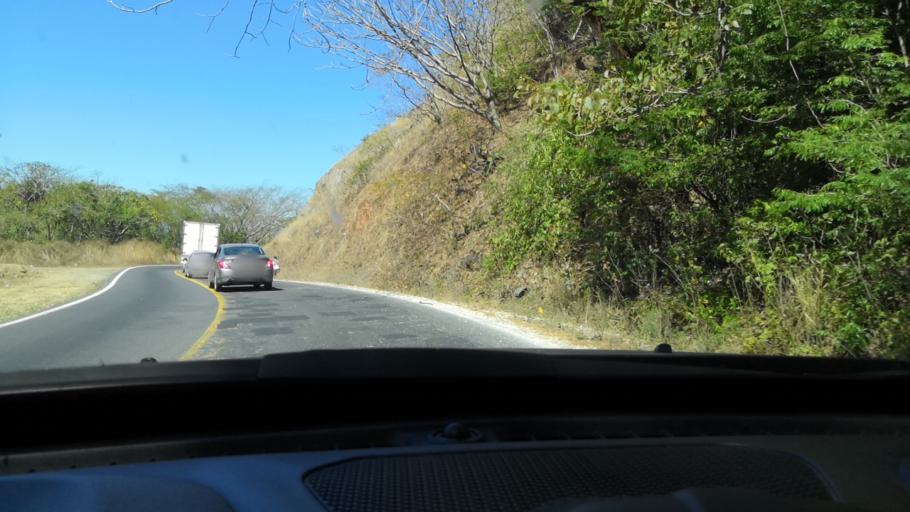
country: MX
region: Nayarit
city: Compostela
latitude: 21.2203
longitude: -104.9975
